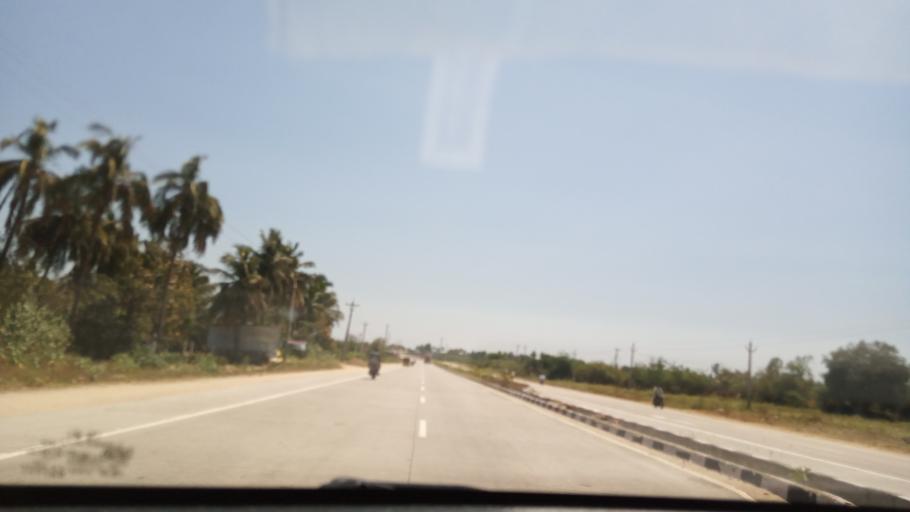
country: IN
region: Andhra Pradesh
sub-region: Chittoor
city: Chittoor
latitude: 13.2034
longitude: 78.9477
